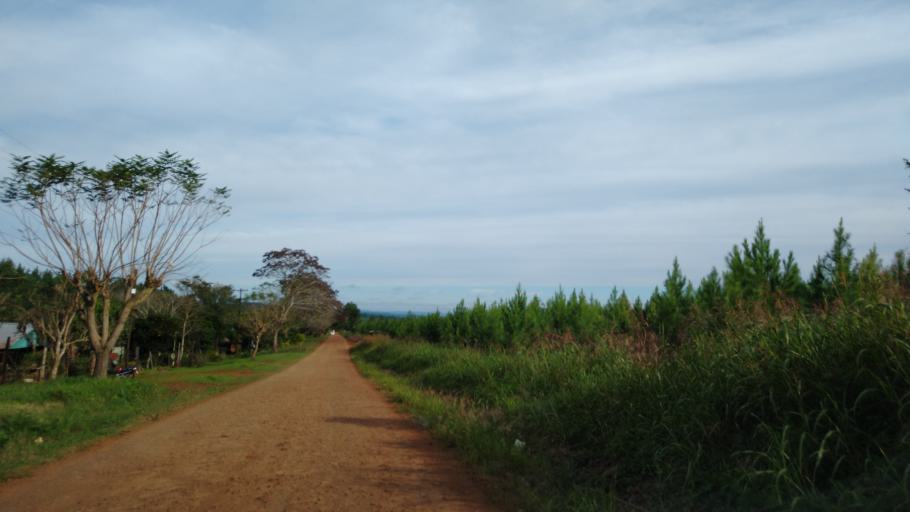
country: AR
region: Misiones
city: Capiovi
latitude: -26.9491
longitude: -55.0965
